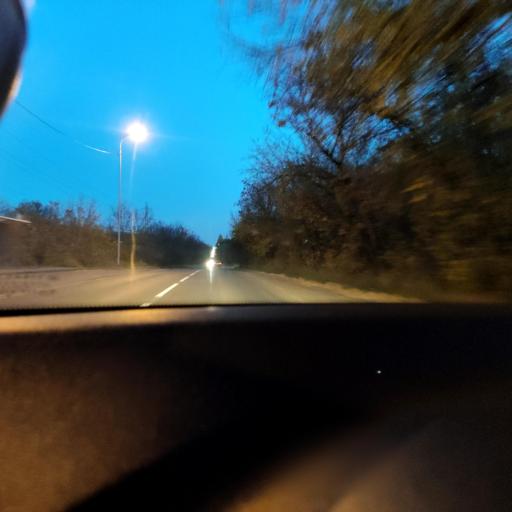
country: RU
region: Samara
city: Petra-Dubrava
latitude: 53.3139
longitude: 50.2724
